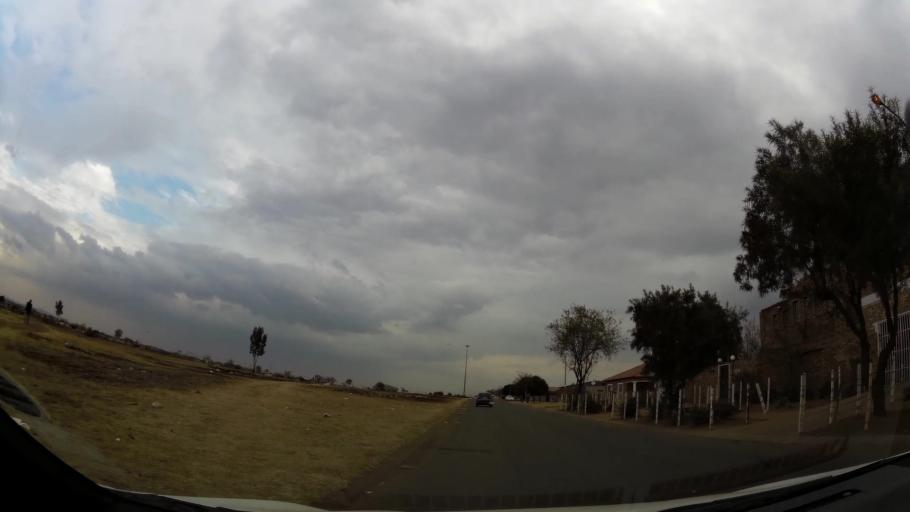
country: ZA
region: Gauteng
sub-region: Ekurhuleni Metropolitan Municipality
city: Germiston
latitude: -26.3829
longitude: 28.1349
